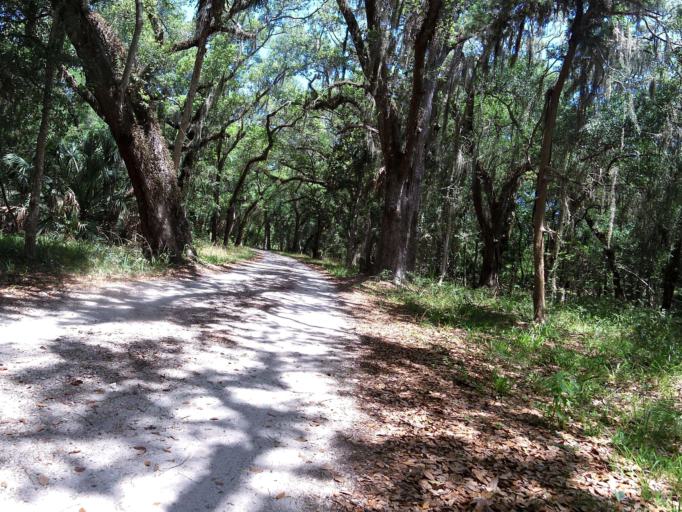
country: US
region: Florida
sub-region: Saint Johns County
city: Villano Beach
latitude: 30.0290
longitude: -81.3367
